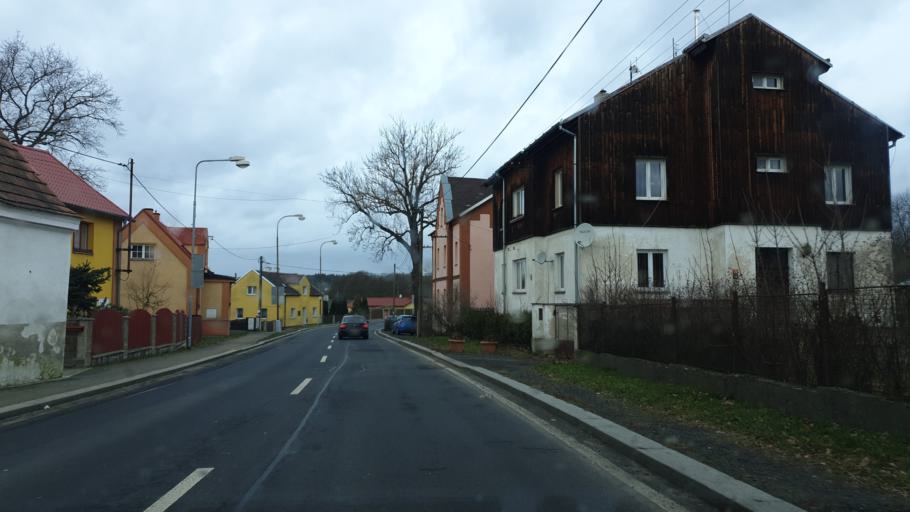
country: CZ
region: Karlovarsky
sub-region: Okres Cheb
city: Frantiskovy Lazne
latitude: 50.1311
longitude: 12.3420
